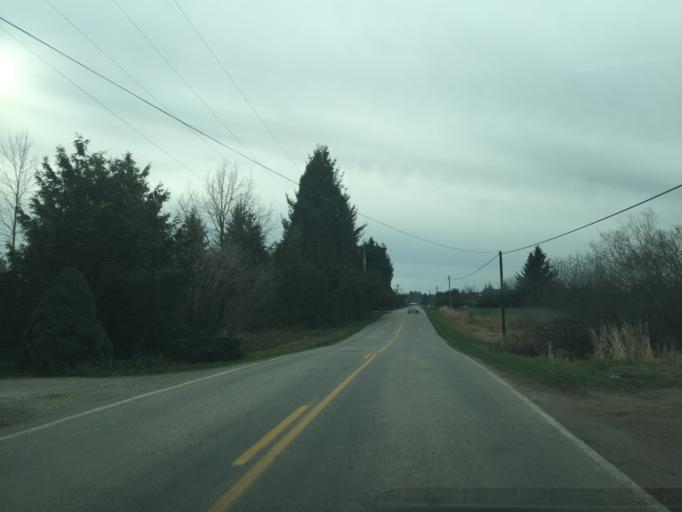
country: US
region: Washington
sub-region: Whatcom County
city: Sumas
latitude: 48.9785
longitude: -122.3038
